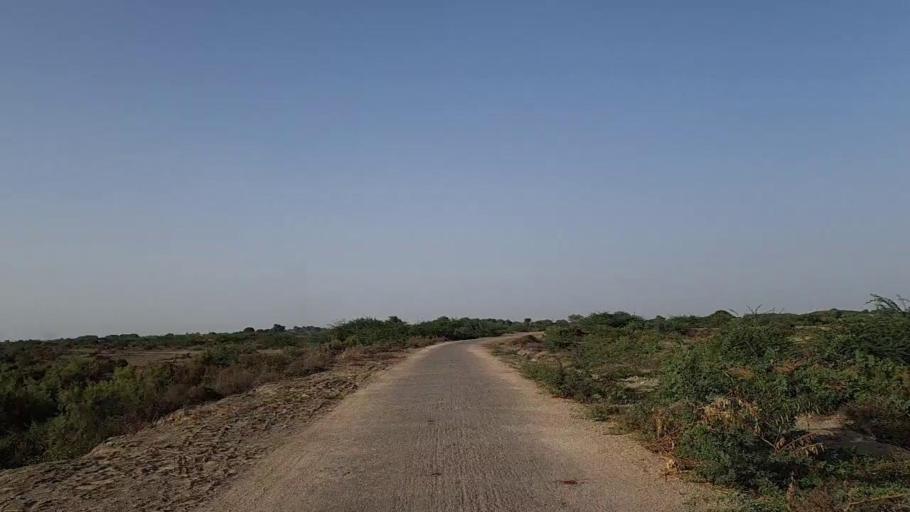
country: PK
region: Sindh
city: Jati
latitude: 24.3075
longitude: 68.1663
